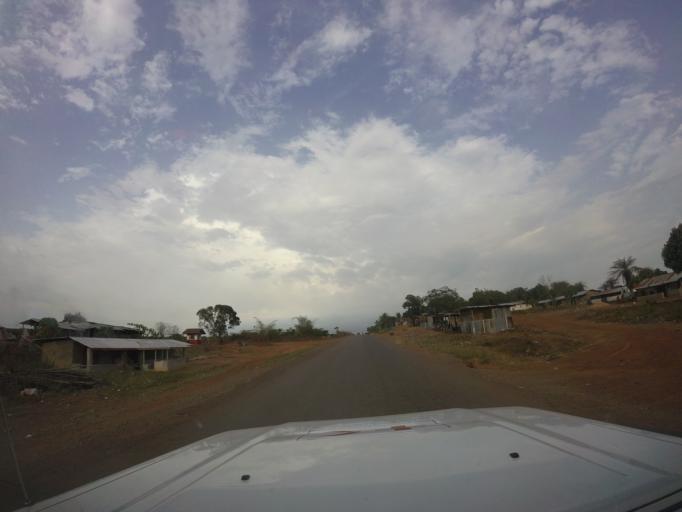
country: LR
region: Bomi
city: Tubmanburg
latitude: 6.7307
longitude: -11.0086
